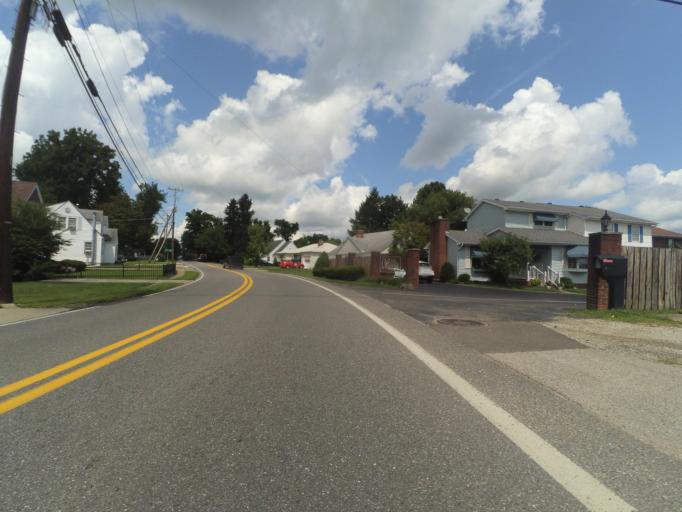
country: US
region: West Virginia
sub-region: Cabell County
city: Pea Ridge
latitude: 38.4132
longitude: -82.3214
